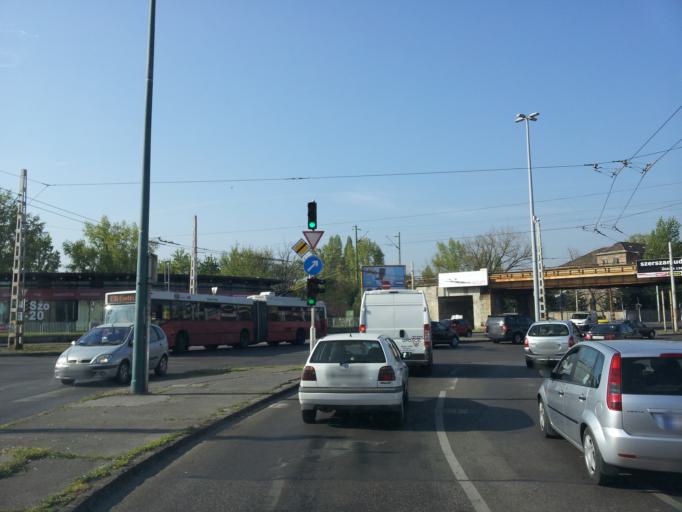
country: HU
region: Budapest
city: Budapest XIV. keruelet
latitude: 47.5012
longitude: 19.1147
